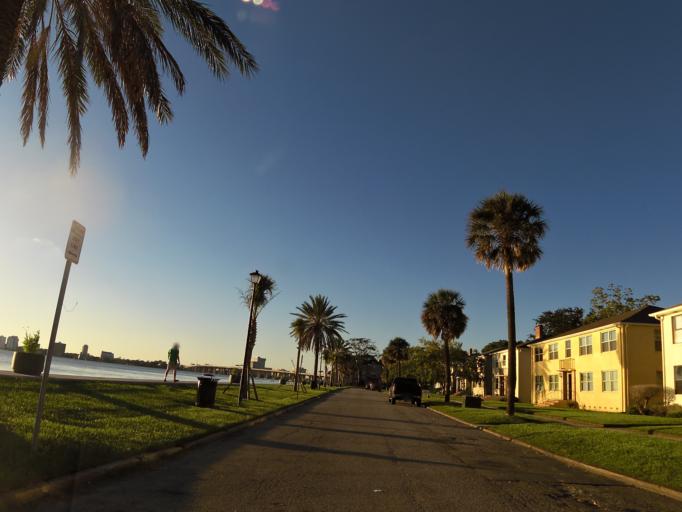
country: US
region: Florida
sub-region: Duval County
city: Jacksonville
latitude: 30.3049
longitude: -81.6601
